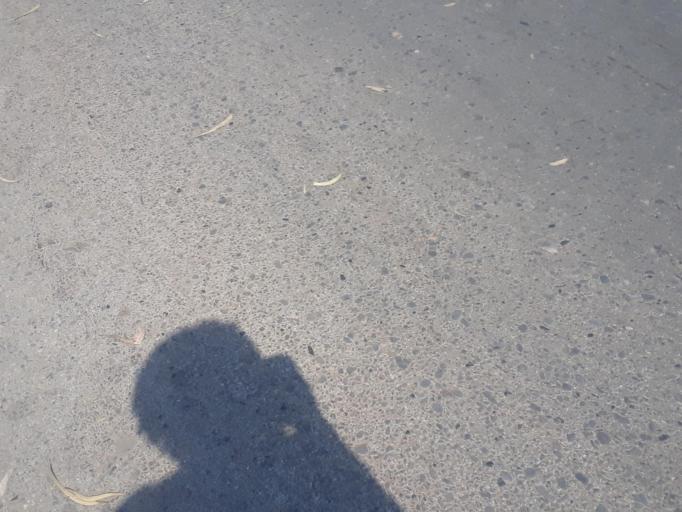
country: ZM
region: Lusaka
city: Lusaka
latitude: -15.3542
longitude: 28.2802
